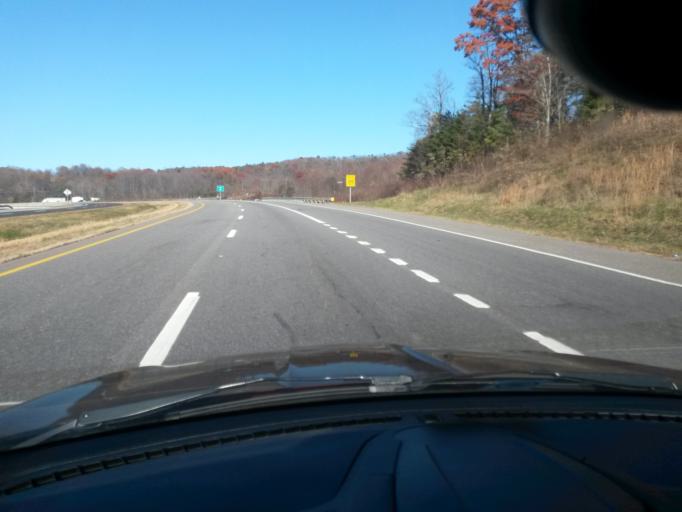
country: US
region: Virginia
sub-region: Patrick County
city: Stuart
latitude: 36.6484
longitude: -80.2673
